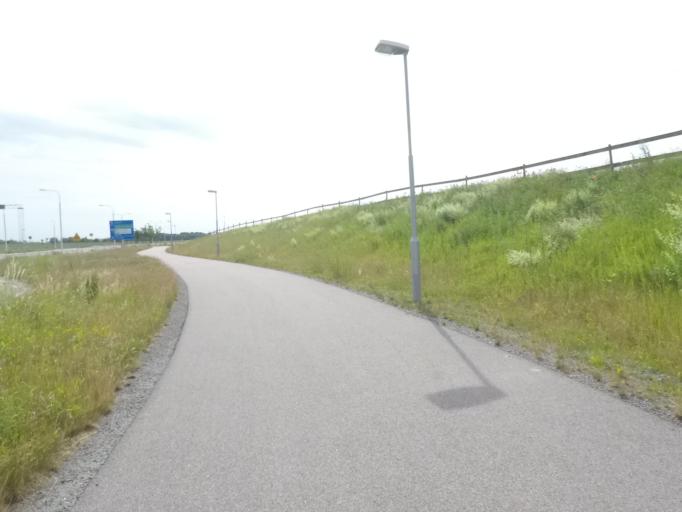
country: SE
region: Skane
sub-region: Malmo
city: Bunkeflostrand
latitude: 55.5453
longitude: 12.9789
